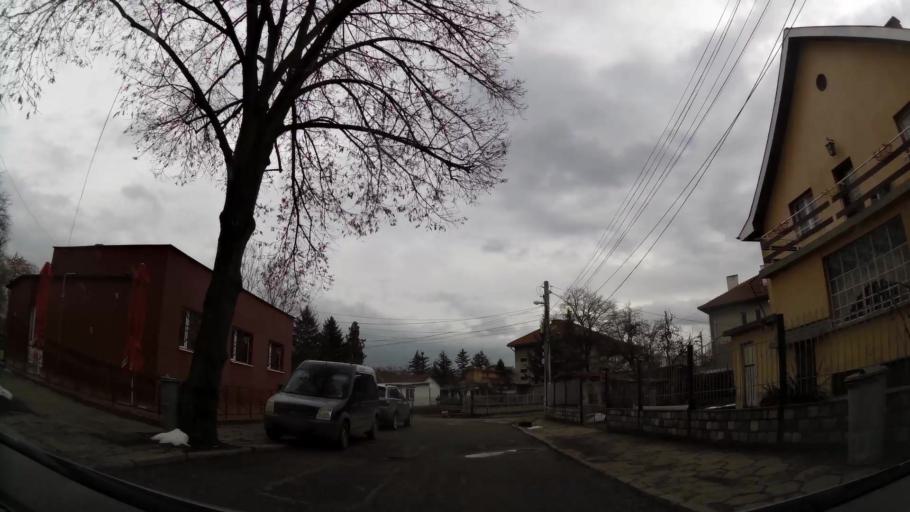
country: BG
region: Sofiya
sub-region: Obshtina Bozhurishte
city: Bozhurishte
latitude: 42.7420
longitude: 23.2661
